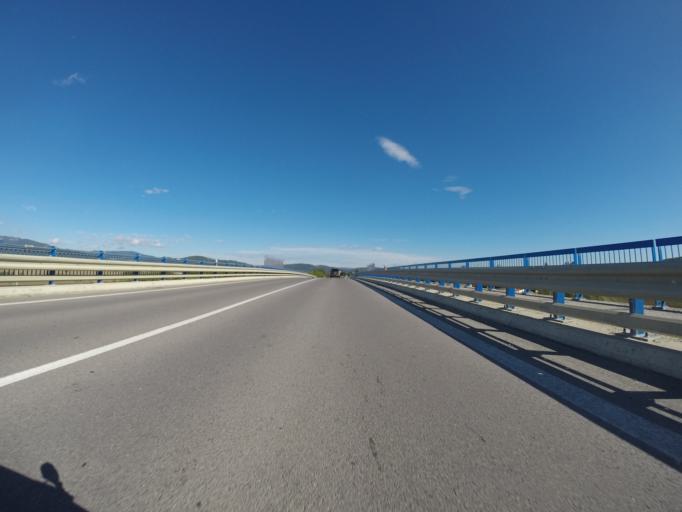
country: SK
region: Nitriansky
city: Ilava
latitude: 49.0225
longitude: 18.2776
